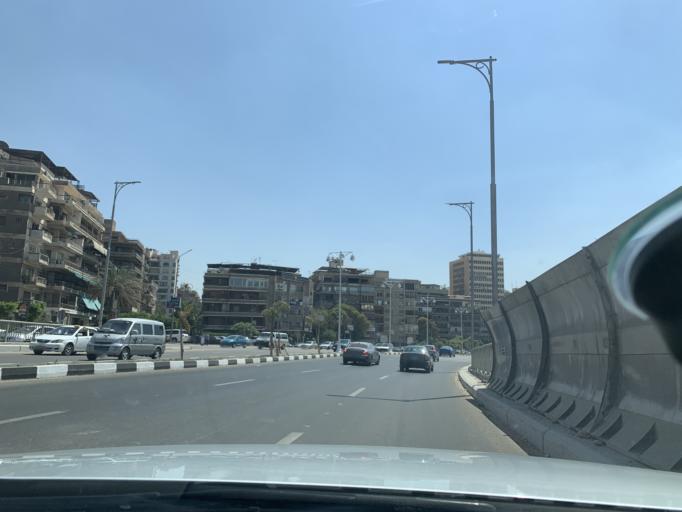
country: EG
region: Muhafazat al Qahirah
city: Cairo
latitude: 30.0857
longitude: 31.3333
